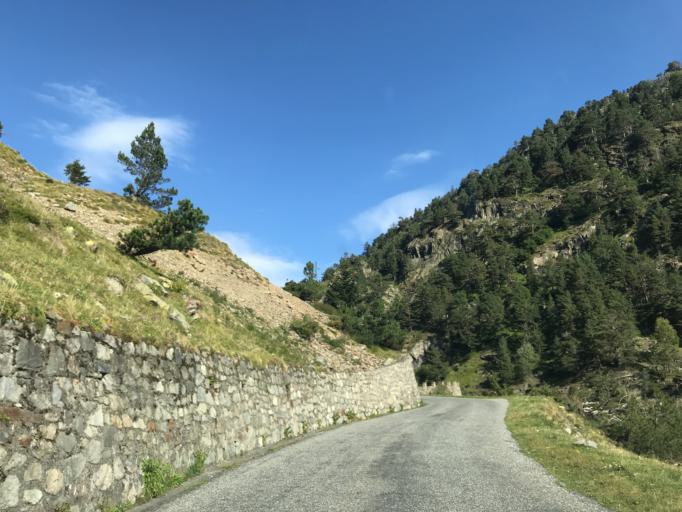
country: FR
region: Midi-Pyrenees
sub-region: Departement des Hautes-Pyrenees
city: Saint-Lary-Soulan
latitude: 42.8215
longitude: 0.1759
